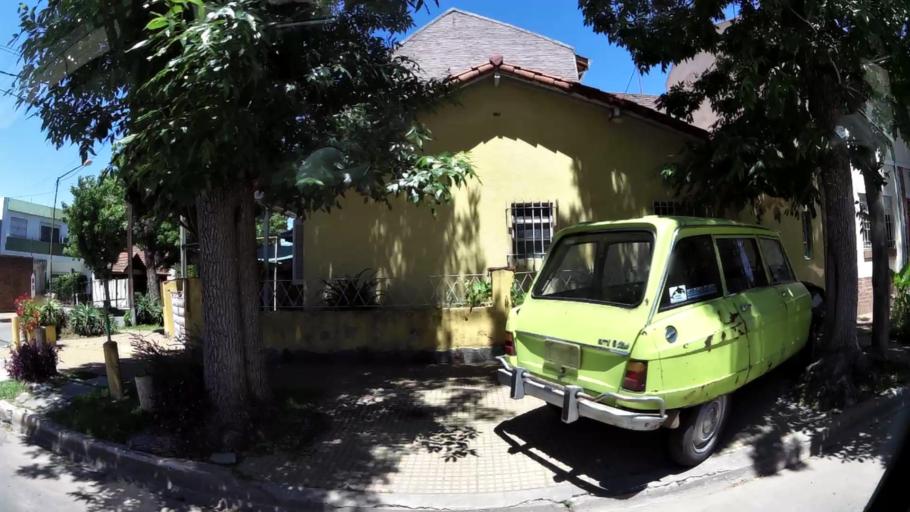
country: AR
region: Buenos Aires
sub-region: Partido de San Isidro
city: San Isidro
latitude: -34.4936
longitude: -58.5149
